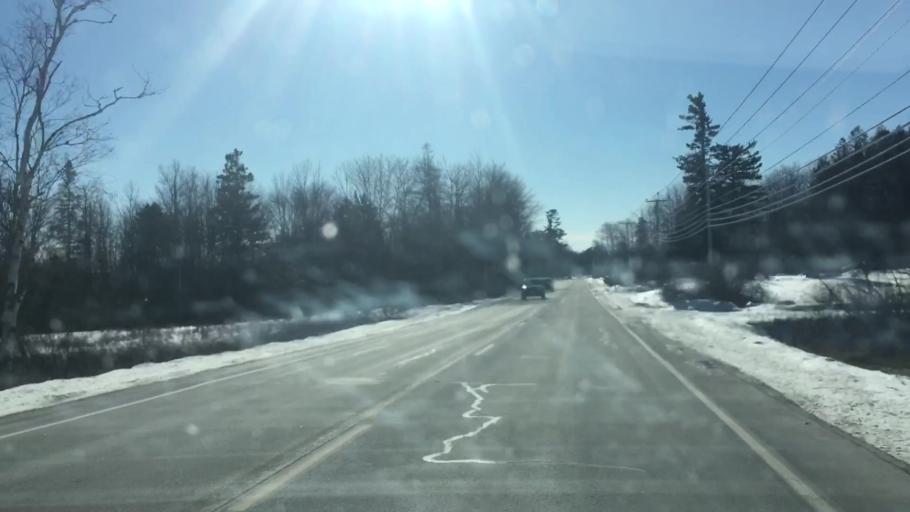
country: US
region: Maine
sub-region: Hancock County
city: Ellsworth
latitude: 44.5020
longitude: -68.4416
